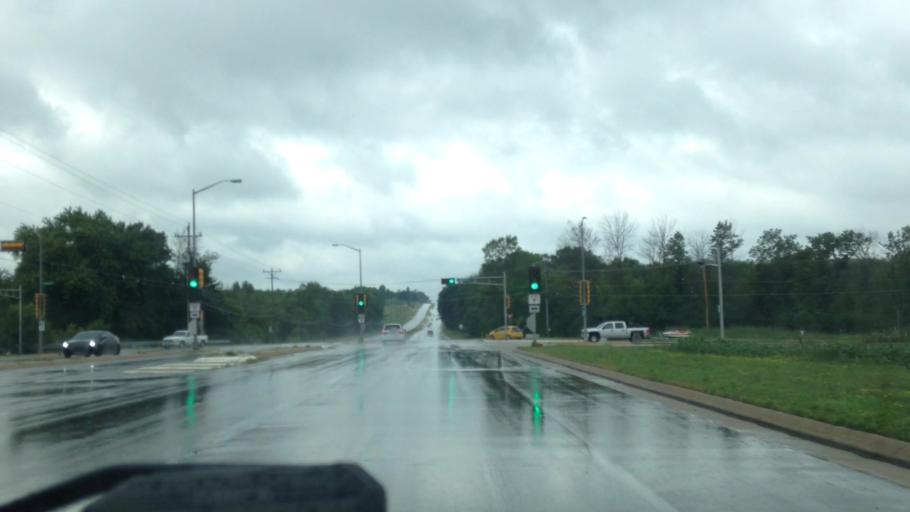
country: US
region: Wisconsin
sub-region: Waukesha County
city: Menomonee Falls
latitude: 43.1924
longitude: -88.1610
